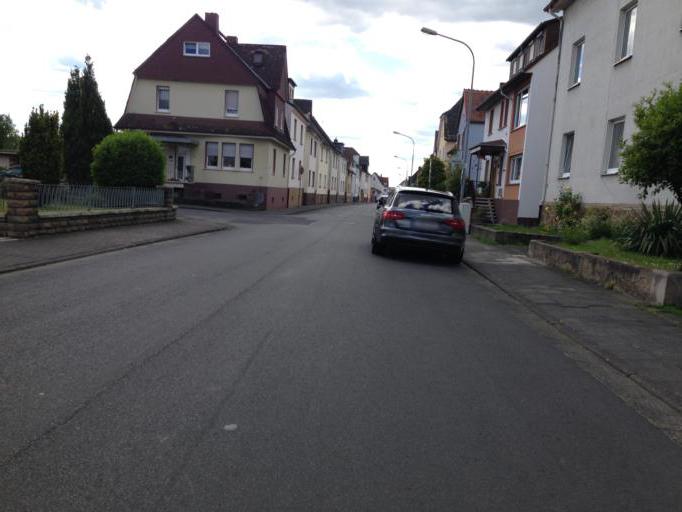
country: DE
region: Hesse
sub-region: Regierungsbezirk Giessen
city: Heuchelheim
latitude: 50.5809
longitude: 8.6327
